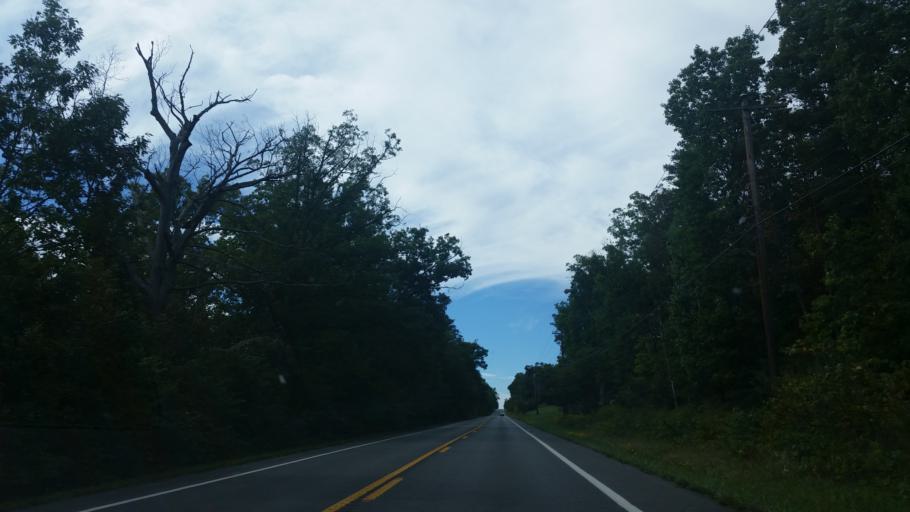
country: US
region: West Virginia
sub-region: Morgan County
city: Berkeley Springs
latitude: 39.5208
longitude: -78.2827
